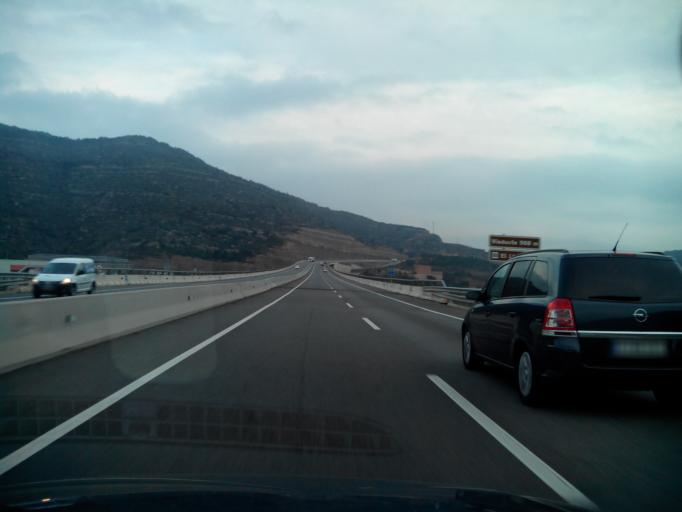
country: ES
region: Catalonia
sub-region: Provincia de Barcelona
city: Puig-reig
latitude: 41.9807
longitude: 1.8863
